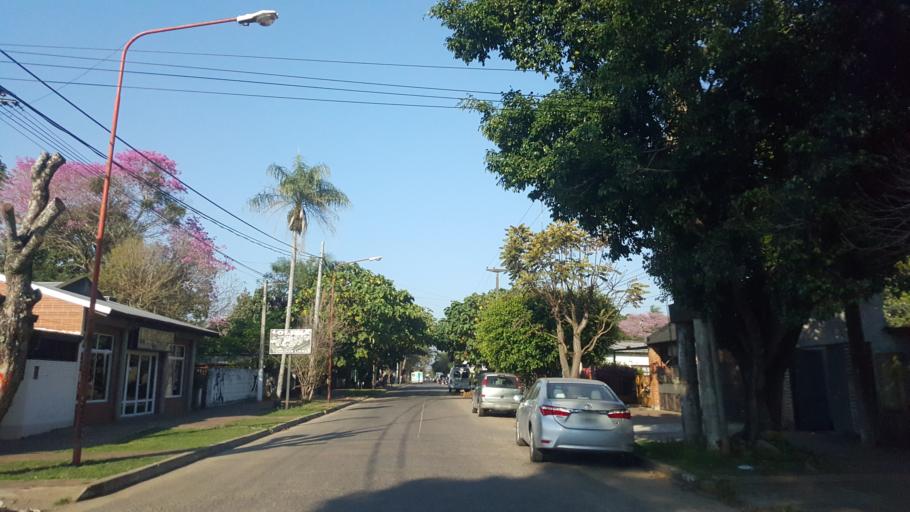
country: AR
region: Corrientes
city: Ituzaingo
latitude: -27.5816
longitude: -56.6841
